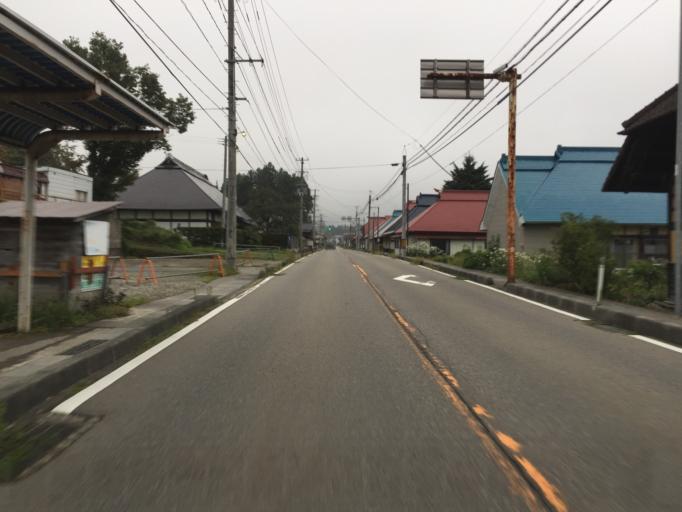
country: JP
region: Fukushima
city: Inawashiro
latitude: 37.3949
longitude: 139.9340
